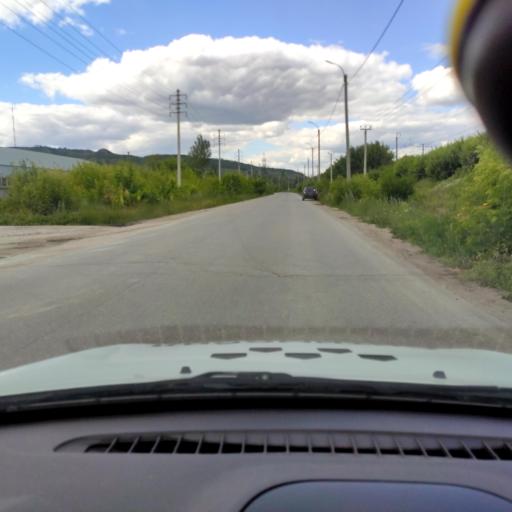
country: RU
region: Samara
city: Zhigulevsk
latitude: 53.4095
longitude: 49.4858
